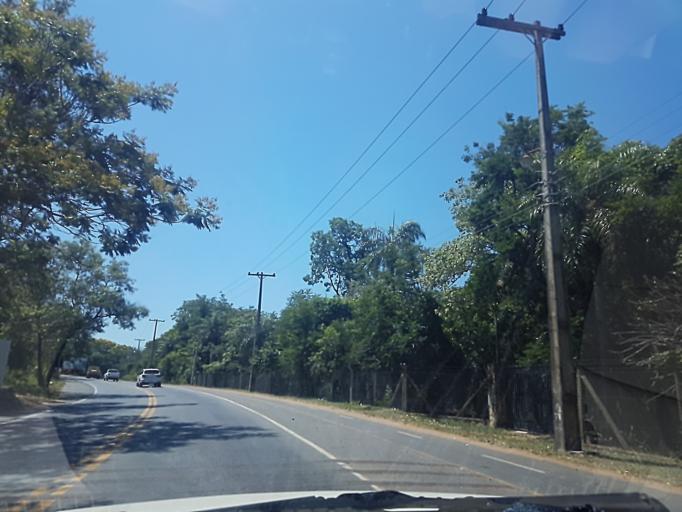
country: PY
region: Cordillera
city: San Bernardino
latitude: -25.2508
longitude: -57.3215
